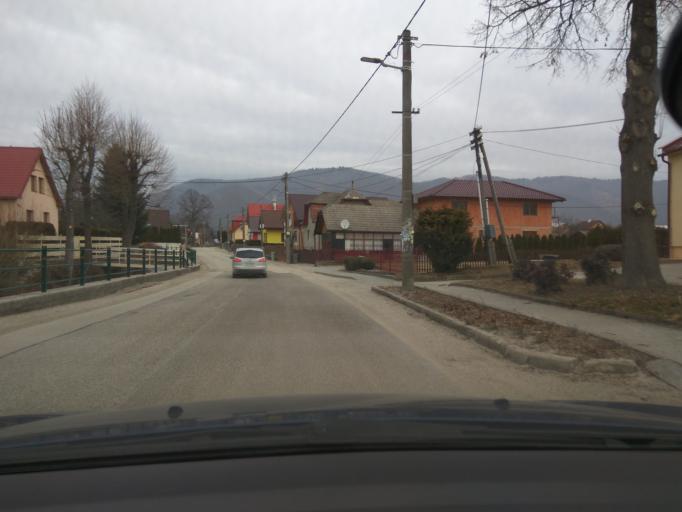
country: SK
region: Zilinsky
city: Rajec
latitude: 49.1146
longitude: 18.6778
